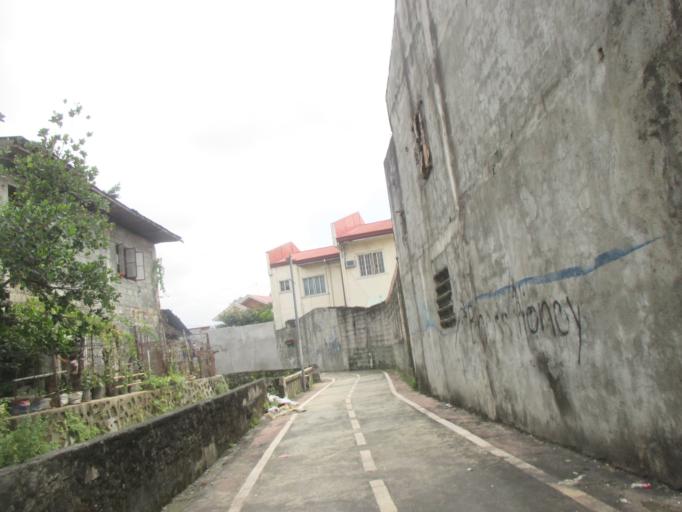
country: PH
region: Calabarzon
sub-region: Province of Rizal
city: Antipolo
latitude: 14.6490
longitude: 121.1075
